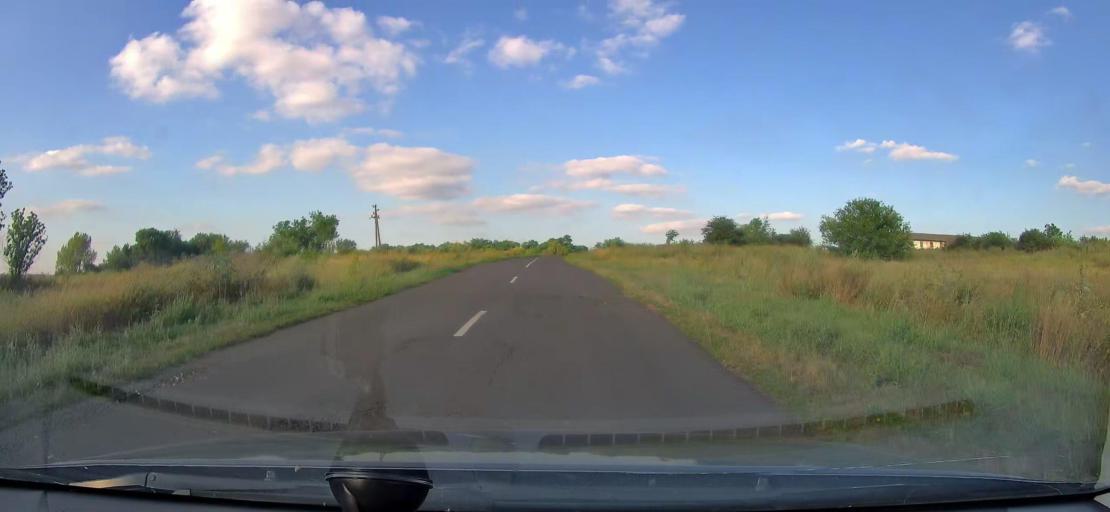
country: RU
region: Kursk
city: Zolotukhino
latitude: 52.0265
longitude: 36.2097
